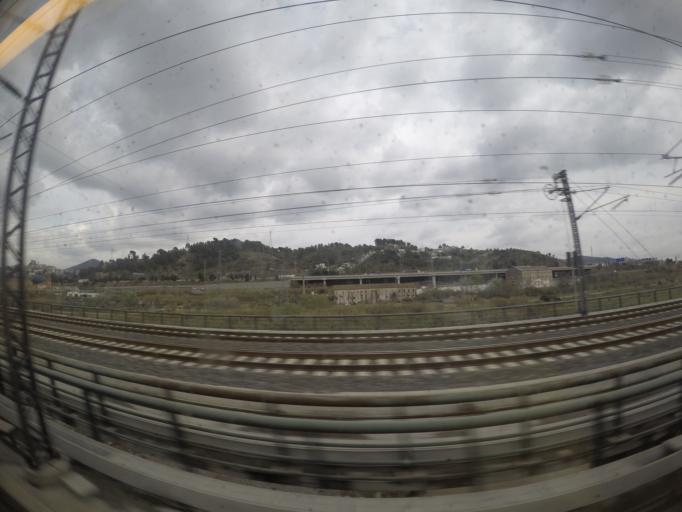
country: ES
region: Catalonia
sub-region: Provincia de Barcelona
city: Palleja
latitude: 41.4237
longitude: 2.0032
